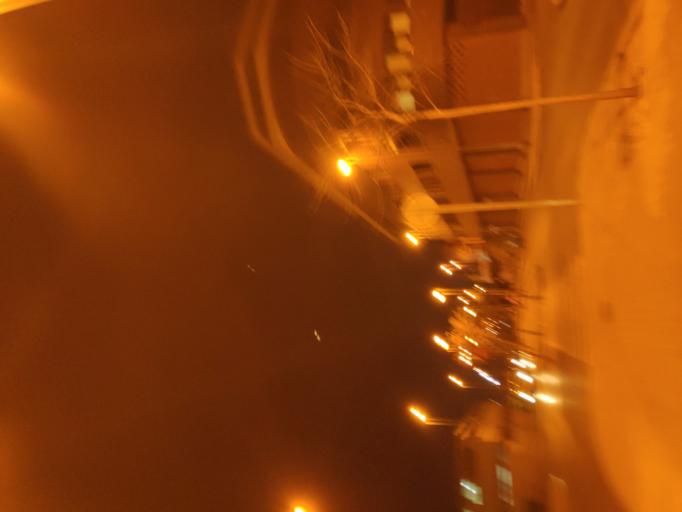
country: ES
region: Valencia
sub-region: Provincia de Castello
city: Castello de la Plana
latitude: 39.9838
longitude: -0.0618
